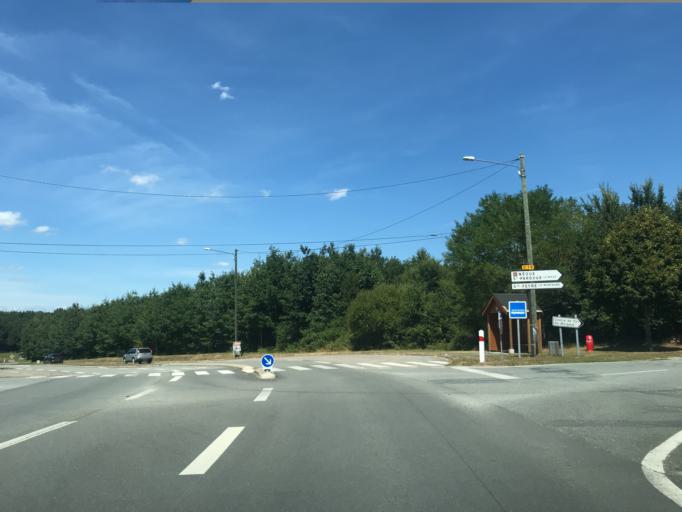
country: FR
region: Limousin
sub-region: Departement de la Creuse
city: Felletin
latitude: 45.8923
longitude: 2.1839
